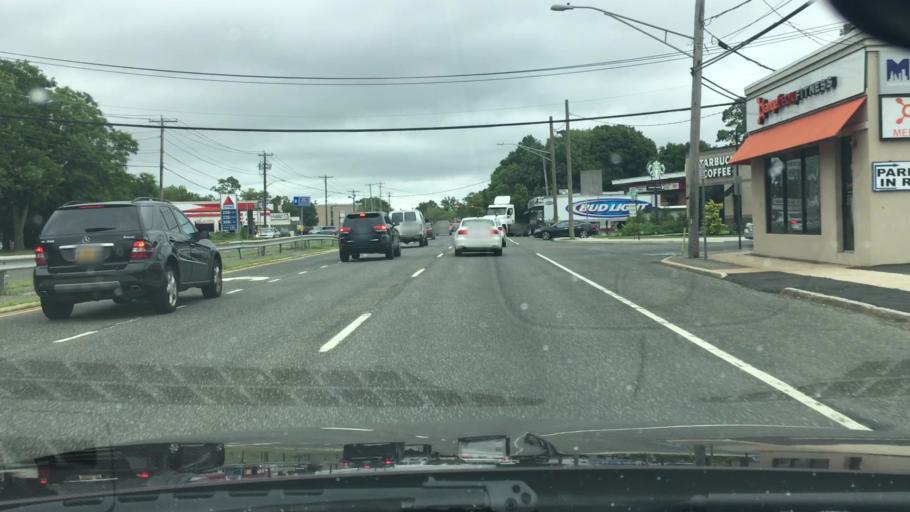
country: US
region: New York
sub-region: Suffolk County
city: South Huntington
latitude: 40.8125
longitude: -73.4097
